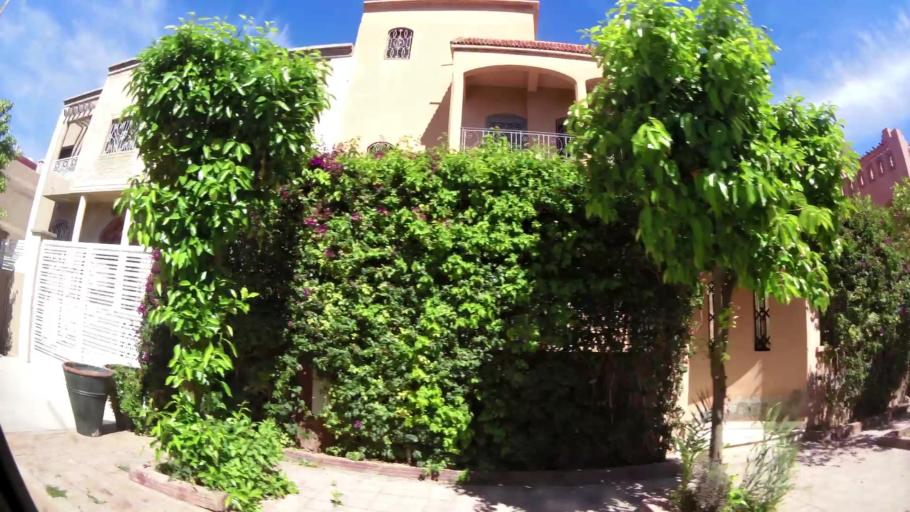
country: MA
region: Marrakech-Tensift-Al Haouz
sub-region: Marrakech
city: Marrakesh
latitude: 31.6783
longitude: -8.0045
